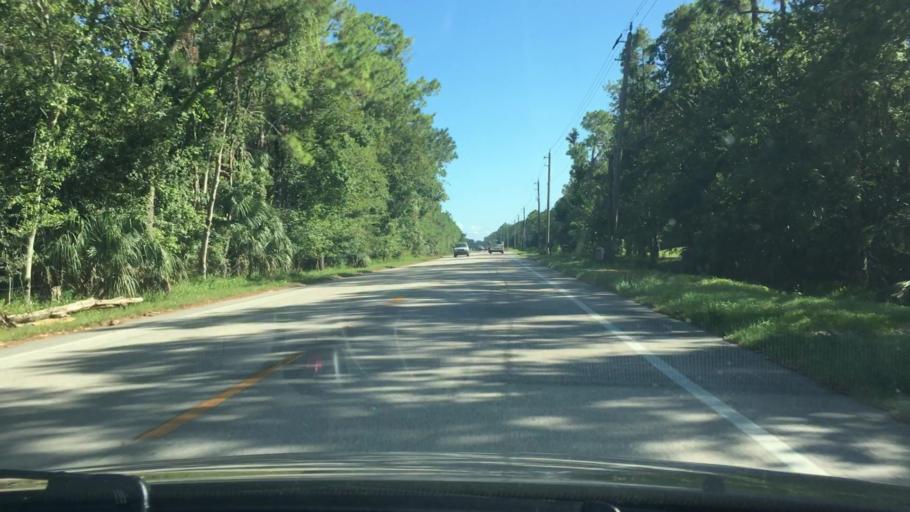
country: US
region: Florida
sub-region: Volusia County
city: South Daytona
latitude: 29.1369
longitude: -81.0767
